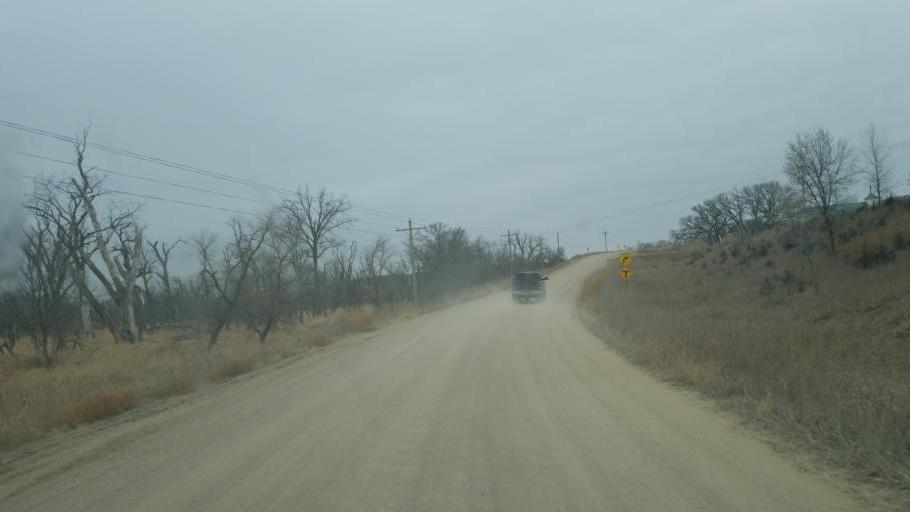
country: US
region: South Dakota
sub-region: Bon Homme County
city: Springfield
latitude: 42.7412
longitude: -97.9285
